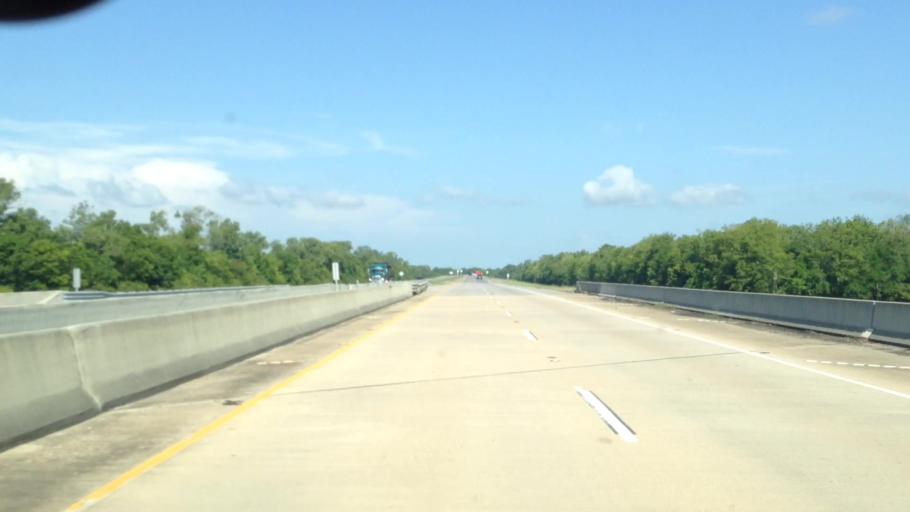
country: US
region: Louisiana
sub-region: Saint Landry Parish
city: Krotz Springs
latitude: 30.5459
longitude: -91.8130
